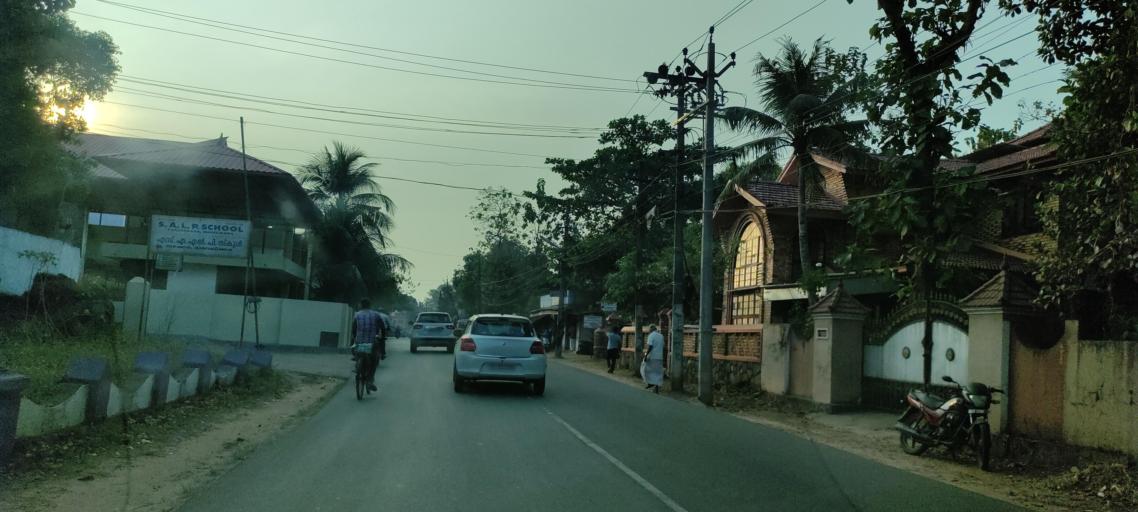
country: IN
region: Kerala
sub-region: Alappuzha
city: Mavelikara
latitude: 9.2564
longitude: 76.5555
